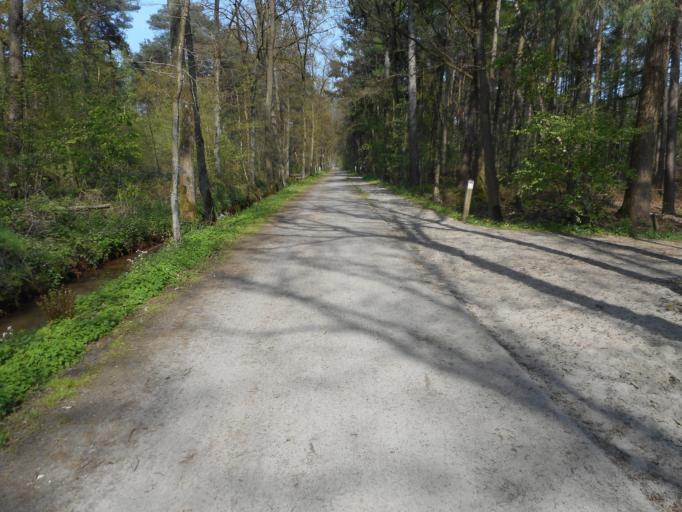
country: BE
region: Flanders
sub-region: Provincie Antwerpen
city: Zandhoven
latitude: 51.2548
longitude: 4.6698
